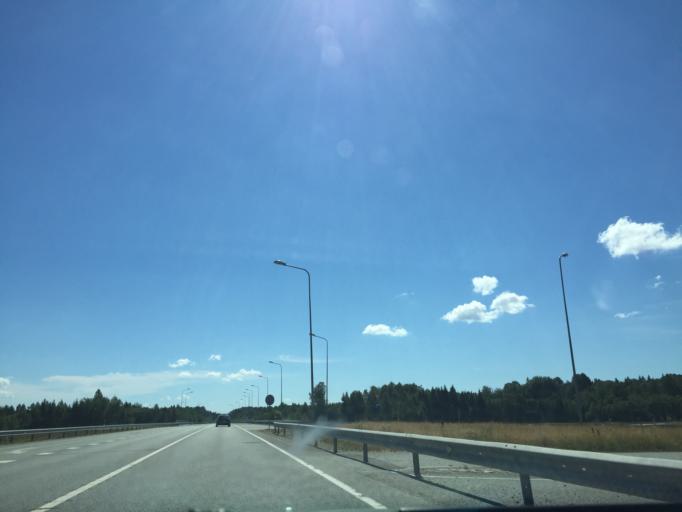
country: LV
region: Skriveri
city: Skriveri
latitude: 56.7315
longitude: 25.1586
